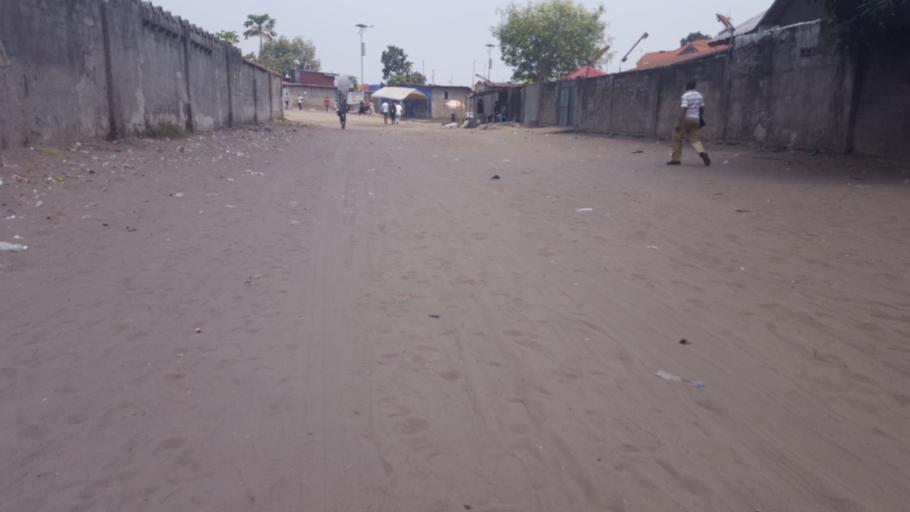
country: CD
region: Kinshasa
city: Masina
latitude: -4.3839
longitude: 15.3537
